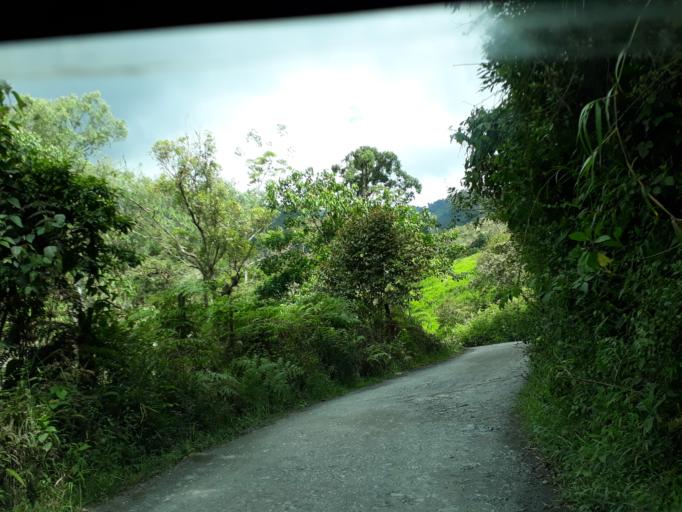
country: CO
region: Cundinamarca
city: Pacho
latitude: 5.2602
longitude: -74.1909
